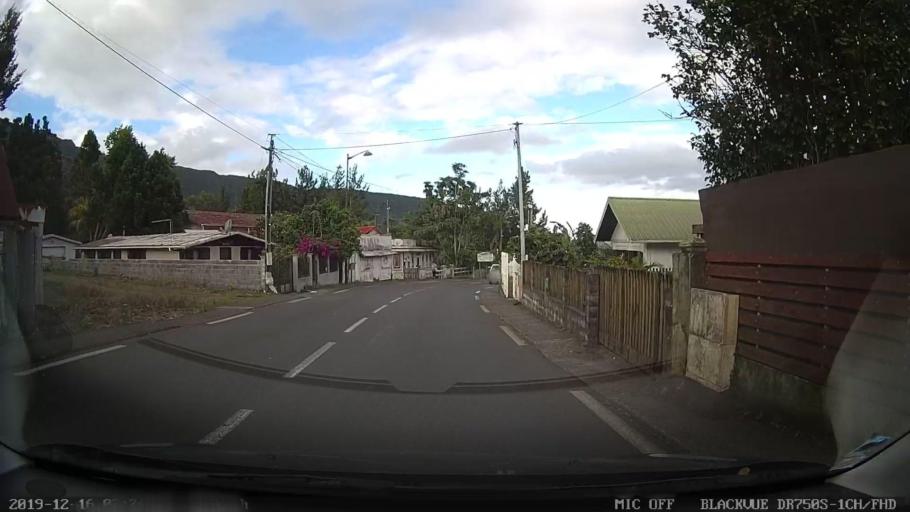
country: RE
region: Reunion
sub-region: Reunion
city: Saint-Benoit
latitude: -21.1392
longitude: 55.6231
